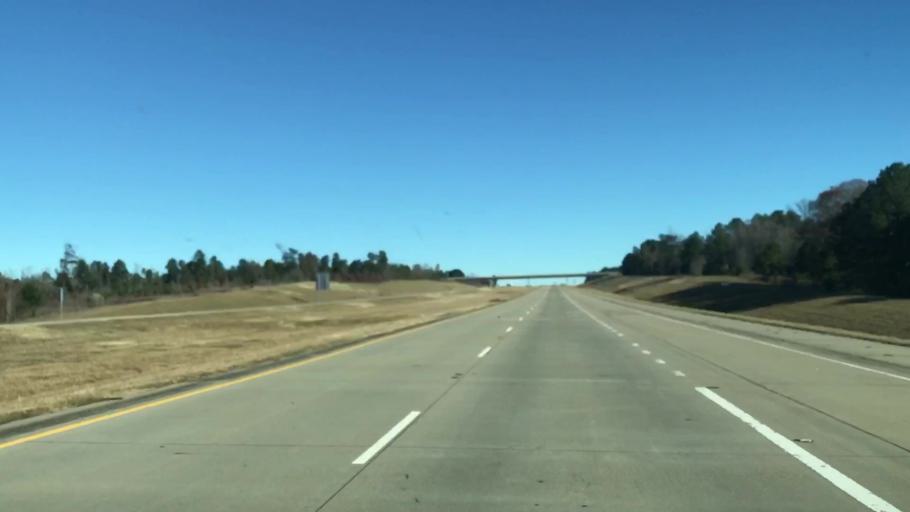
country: US
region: Louisiana
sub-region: Caddo Parish
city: Vivian
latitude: 33.0021
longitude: -93.9074
